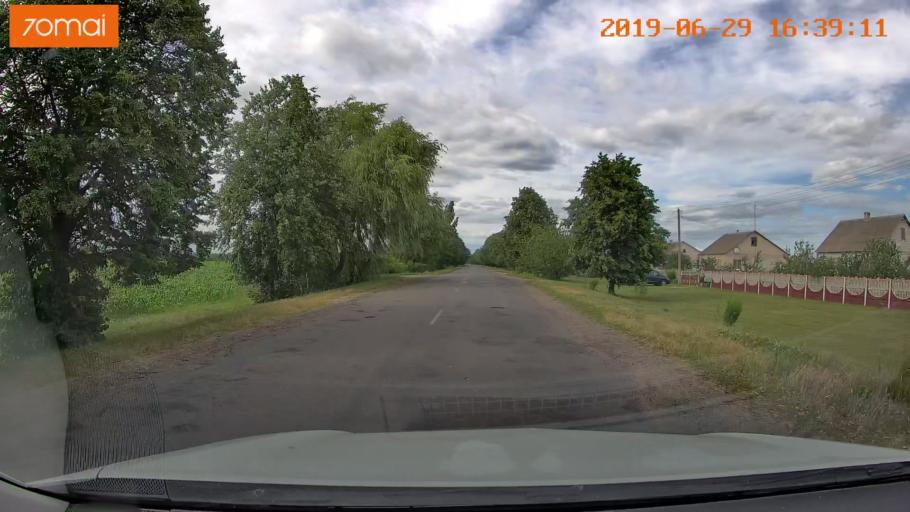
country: BY
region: Brest
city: Luninyets
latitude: 52.2395
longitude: 27.0158
